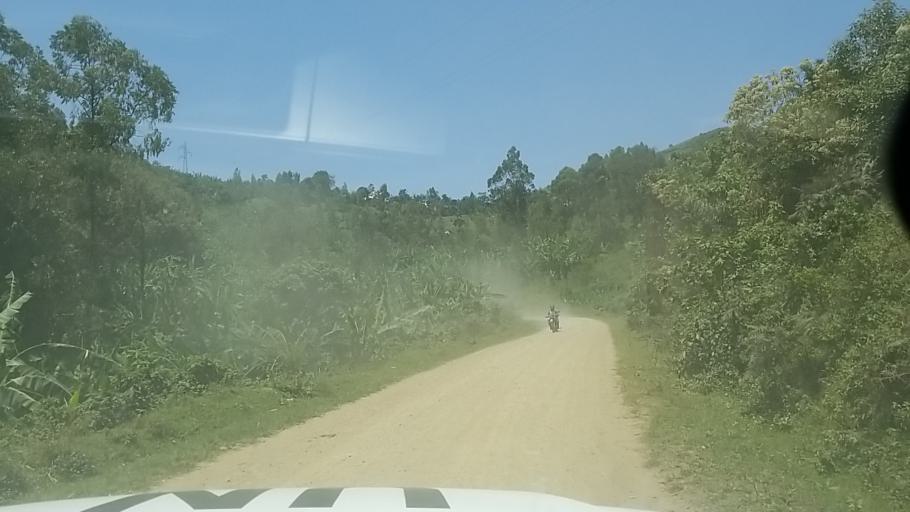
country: CD
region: Nord Kivu
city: Sake
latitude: -1.7764
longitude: 29.0094
